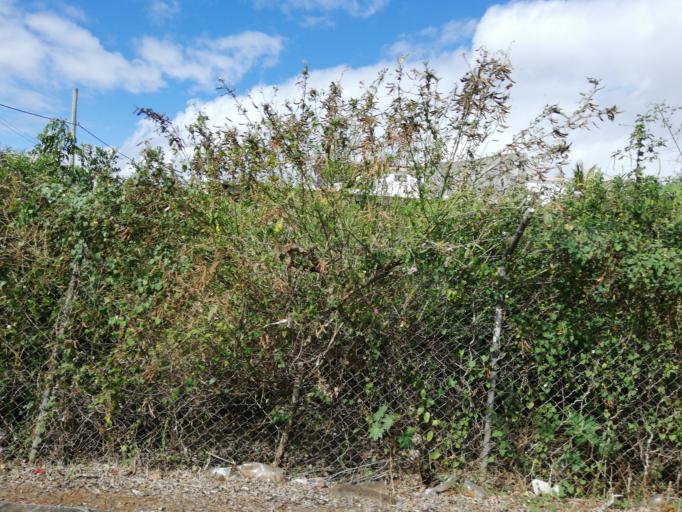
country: MU
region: Black River
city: Petite Riviere
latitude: -20.2175
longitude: 57.4602
